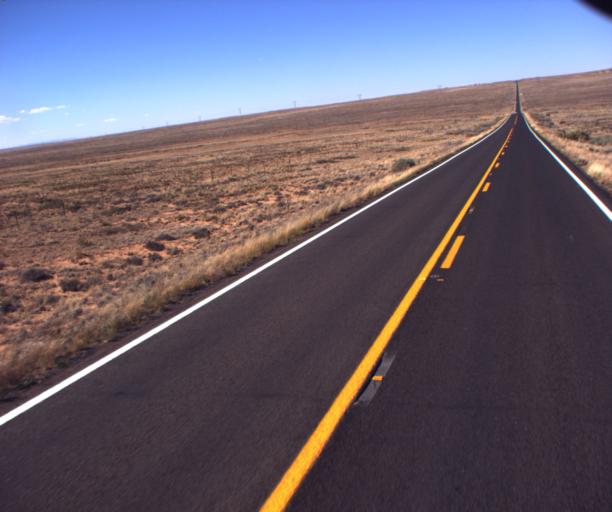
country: US
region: Arizona
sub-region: Coconino County
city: Tuba City
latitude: 35.9388
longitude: -110.9044
